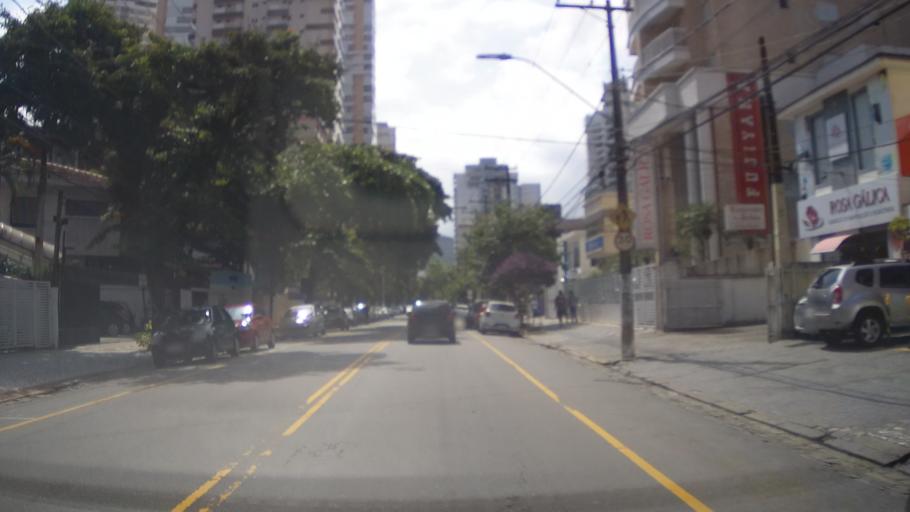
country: BR
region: Sao Paulo
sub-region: Santos
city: Santos
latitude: -23.9655
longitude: -46.3346
